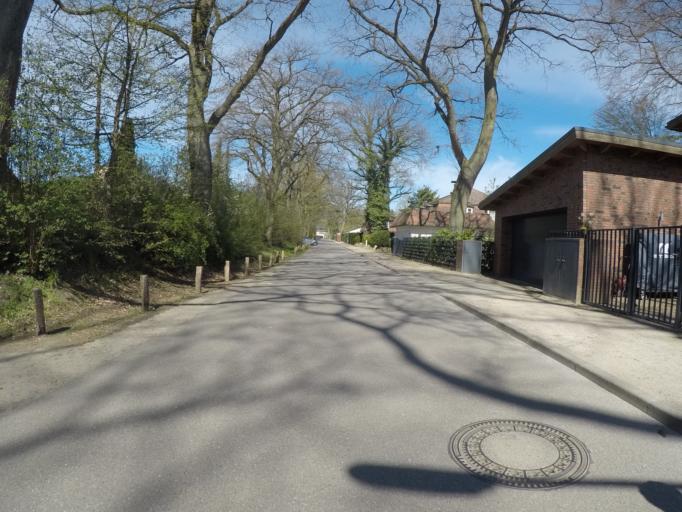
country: DE
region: Hamburg
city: Lemsahl-Mellingstedt
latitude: 53.6735
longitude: 10.1027
